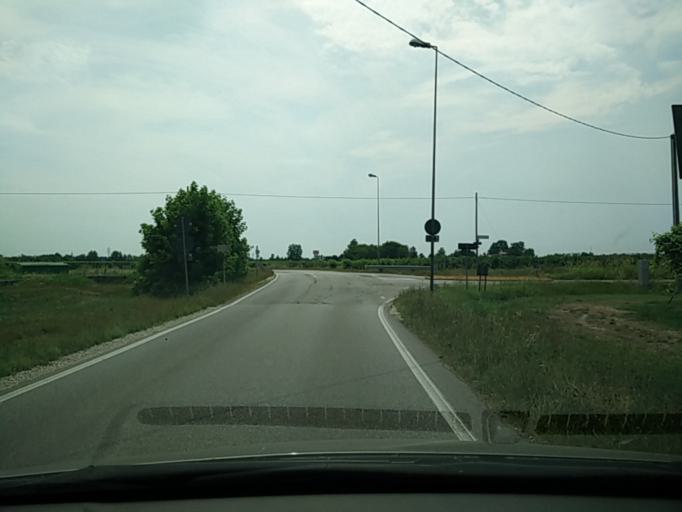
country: IT
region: Veneto
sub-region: Provincia di Treviso
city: Carbonera
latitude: 45.7021
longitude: 12.2992
